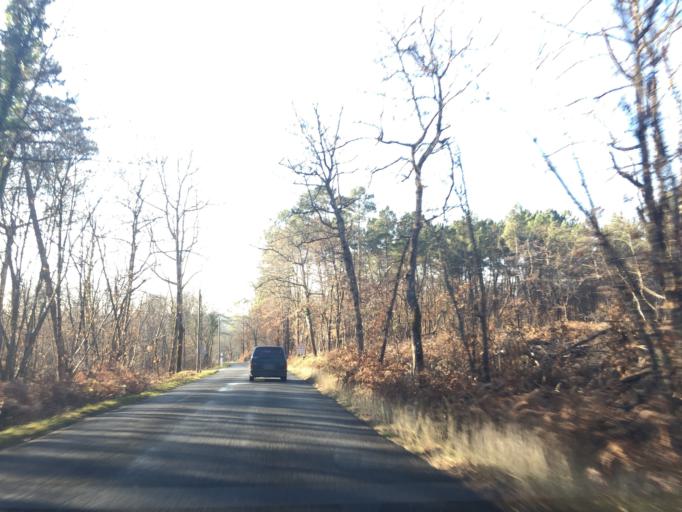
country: FR
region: Aquitaine
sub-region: Departement de la Dordogne
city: Neuvic
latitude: 45.1368
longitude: 0.4679
